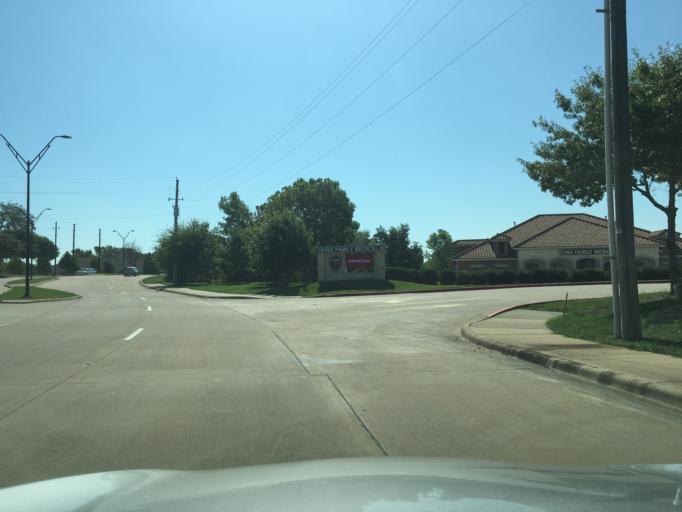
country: US
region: Texas
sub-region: Dallas County
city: Sachse
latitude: 32.9683
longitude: -96.6066
